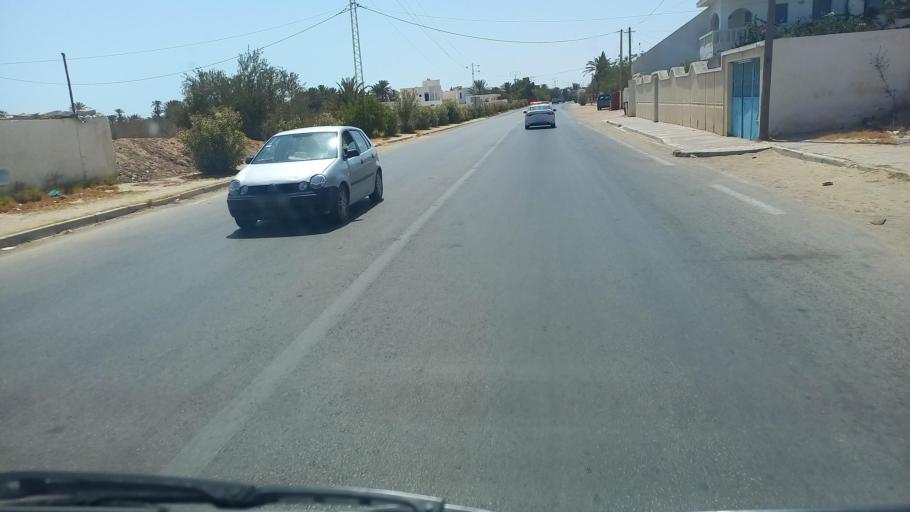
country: TN
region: Madanin
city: Houmt Souk
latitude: 33.7964
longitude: 10.8857
